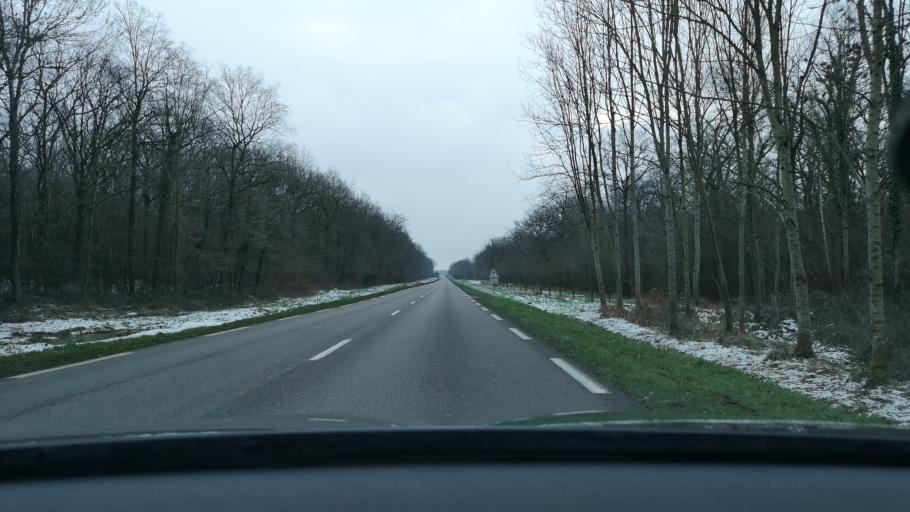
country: FR
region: Bourgogne
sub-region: Departement de Saone-et-Loire
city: Ouroux-sur-Saone
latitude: 46.7771
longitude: 4.9536
